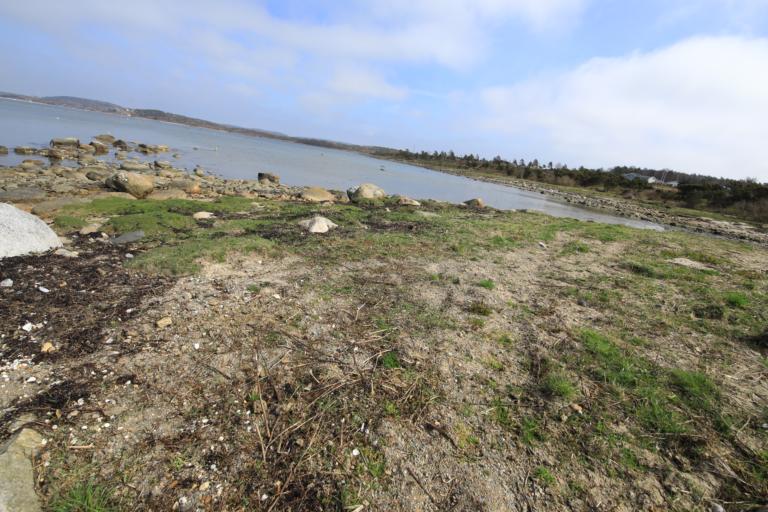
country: SE
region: Halland
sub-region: Kungsbacka Kommun
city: Frillesas
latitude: 57.2818
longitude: 12.1509
